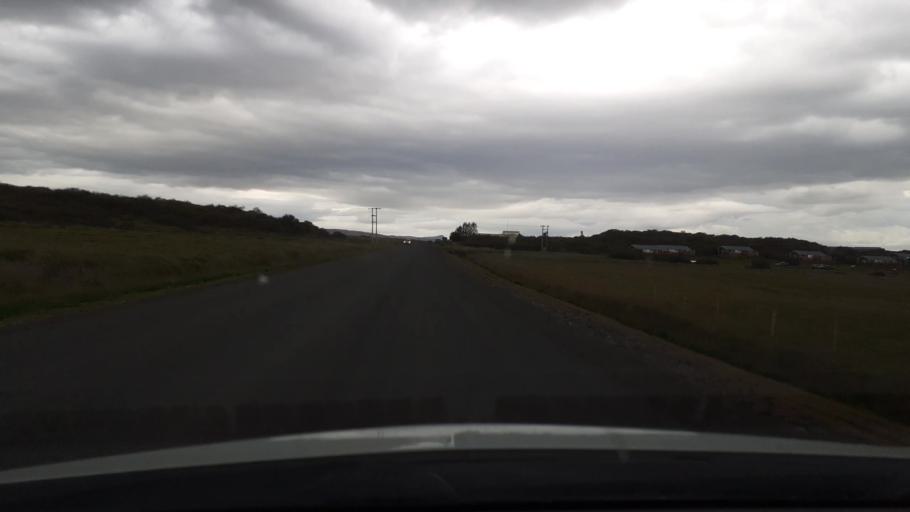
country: IS
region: West
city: Borgarnes
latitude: 64.6715
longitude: -21.7014
